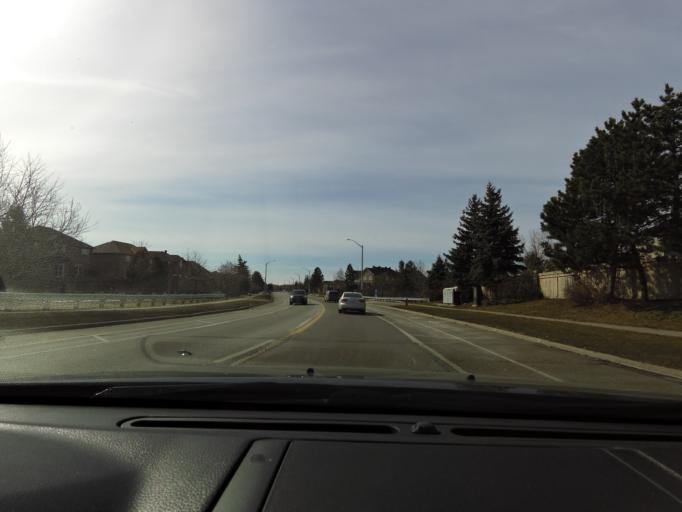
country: CA
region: Ontario
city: Brampton
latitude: 43.7368
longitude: -79.7623
